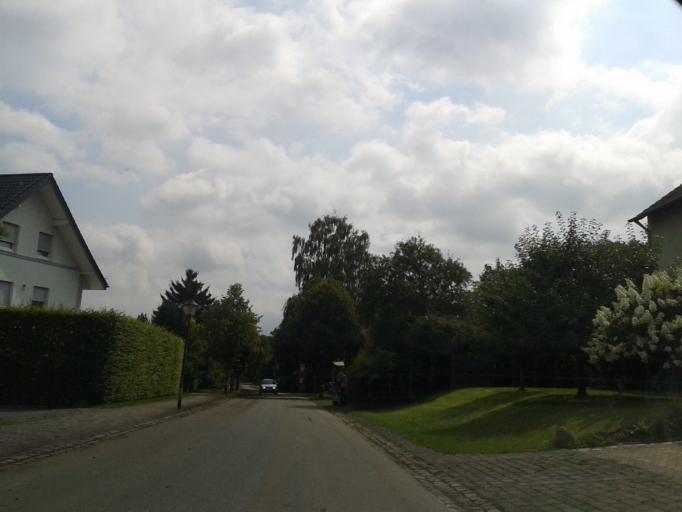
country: DE
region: North Rhine-Westphalia
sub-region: Regierungsbezirk Detmold
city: Dorentrup
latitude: 51.9896
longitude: 8.9891
